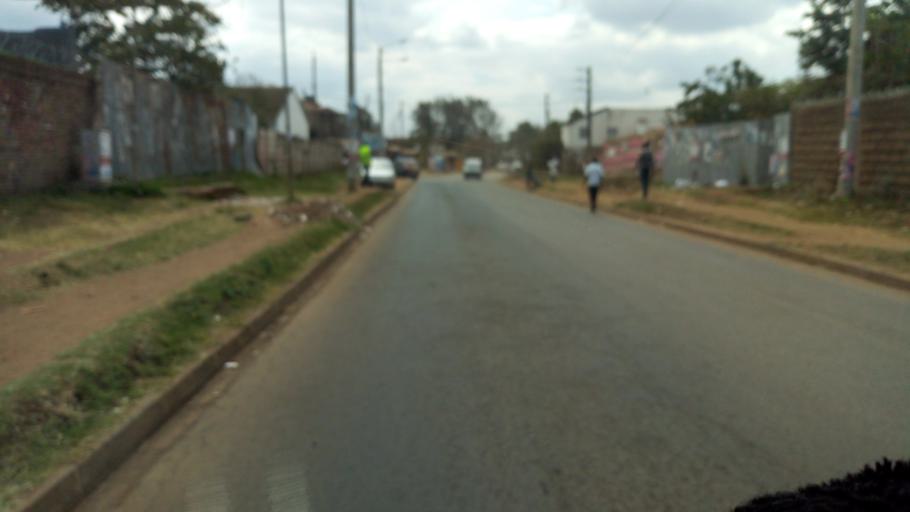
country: KE
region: Nairobi Area
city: Nairobi
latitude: -1.3262
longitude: 36.7854
